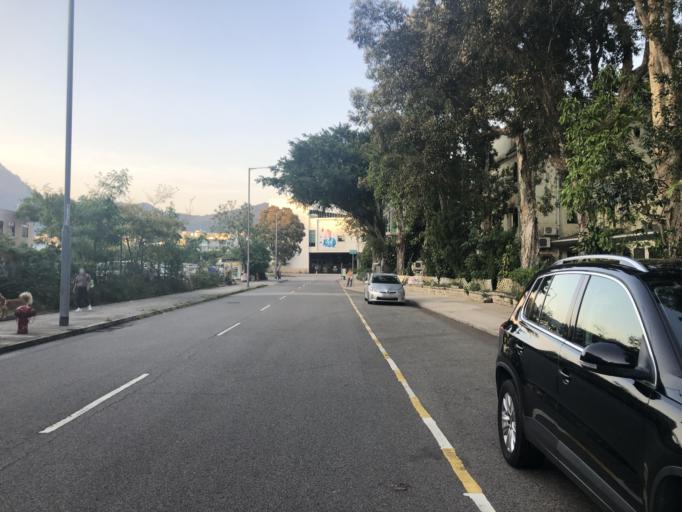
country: HK
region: Sai Kung
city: Sai Kung
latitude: 22.3767
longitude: 114.2735
